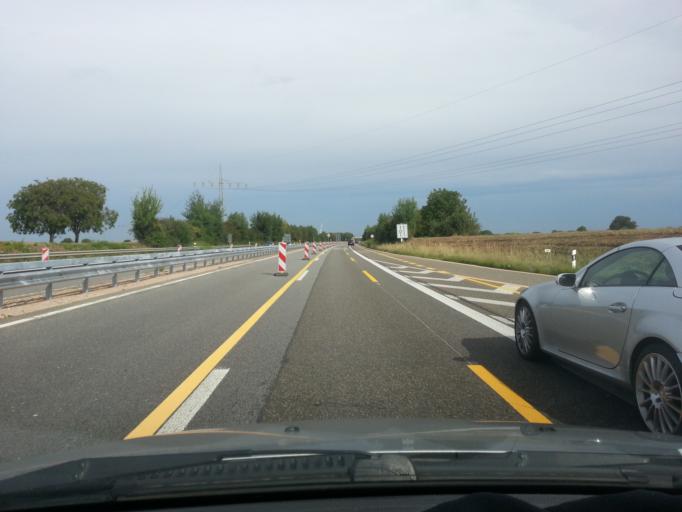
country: DE
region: Rheinland-Pfalz
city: Meckenheim
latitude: 49.3780
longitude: 8.2229
